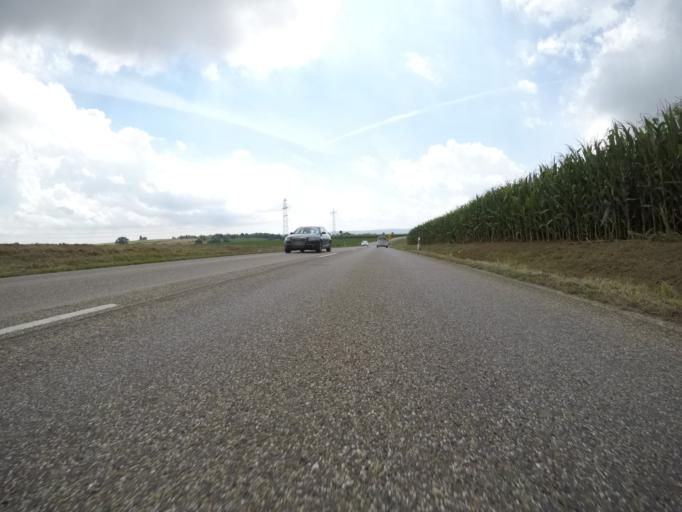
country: DE
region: Baden-Wuerttemberg
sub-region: Regierungsbezirk Stuttgart
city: Schwieberdingen
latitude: 48.8709
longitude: 9.0981
